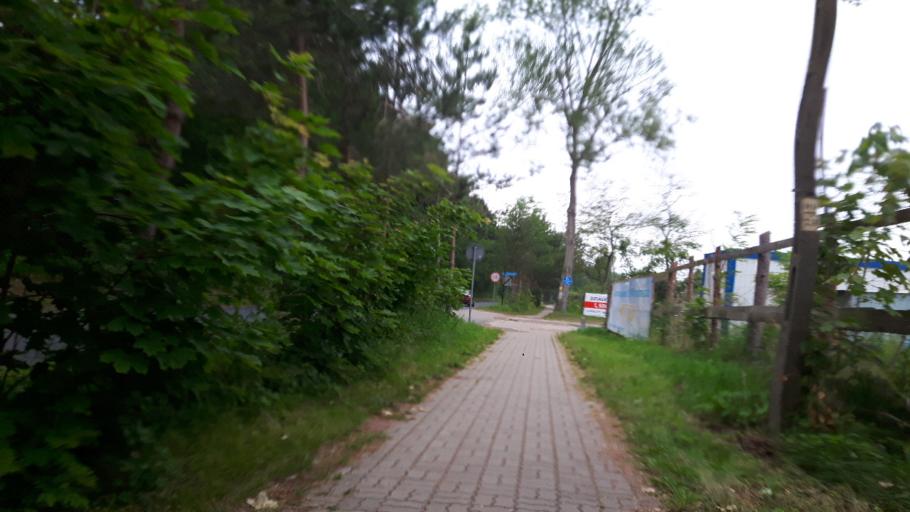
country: PL
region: West Pomeranian Voivodeship
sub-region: Powiat koszalinski
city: Mielno
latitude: 54.2772
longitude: 16.1148
